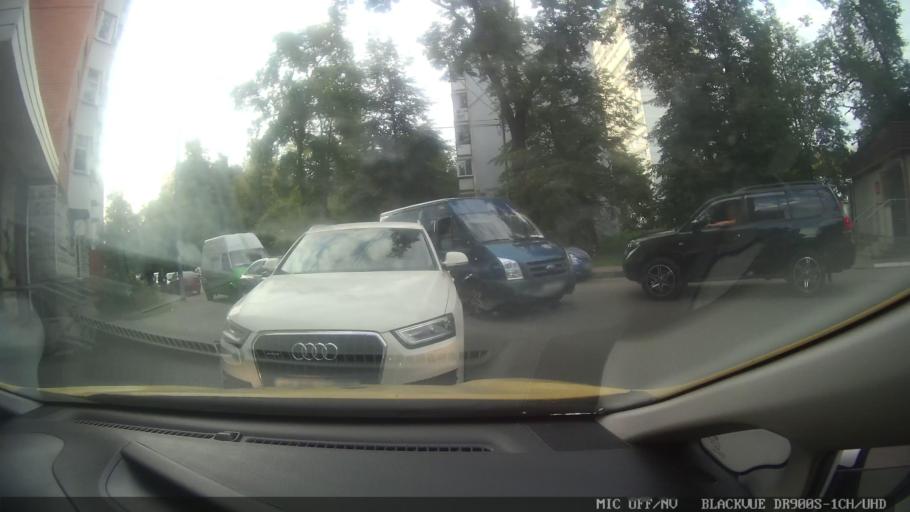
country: RU
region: Moscow
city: Vatutino
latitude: 55.8574
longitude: 37.6992
